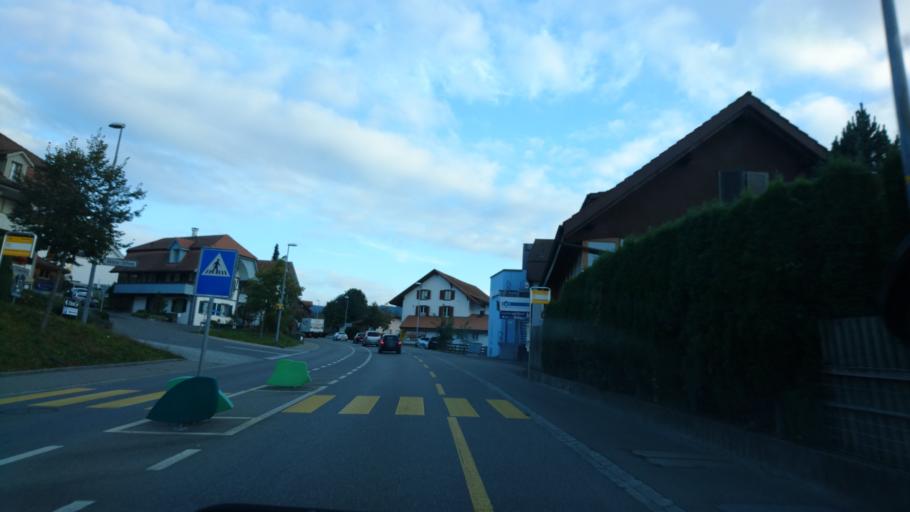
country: CH
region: Bern
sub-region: Bern-Mittelland District
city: Worb
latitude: 46.9189
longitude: 7.5826
